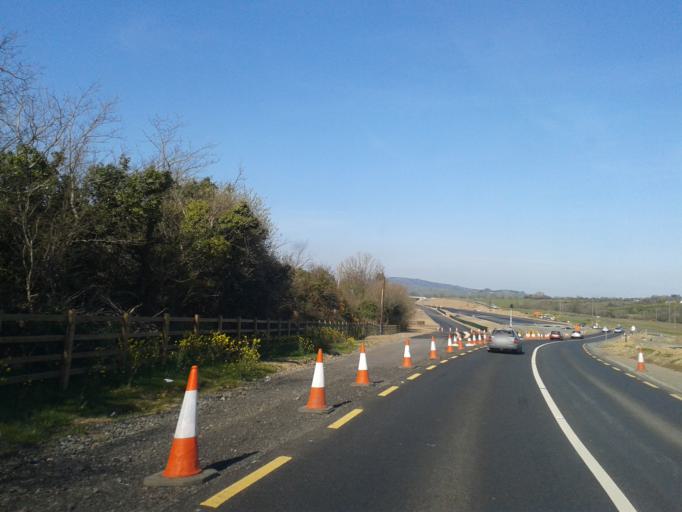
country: IE
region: Leinster
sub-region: Wicklow
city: Arklow
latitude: 52.8503
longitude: -6.1091
